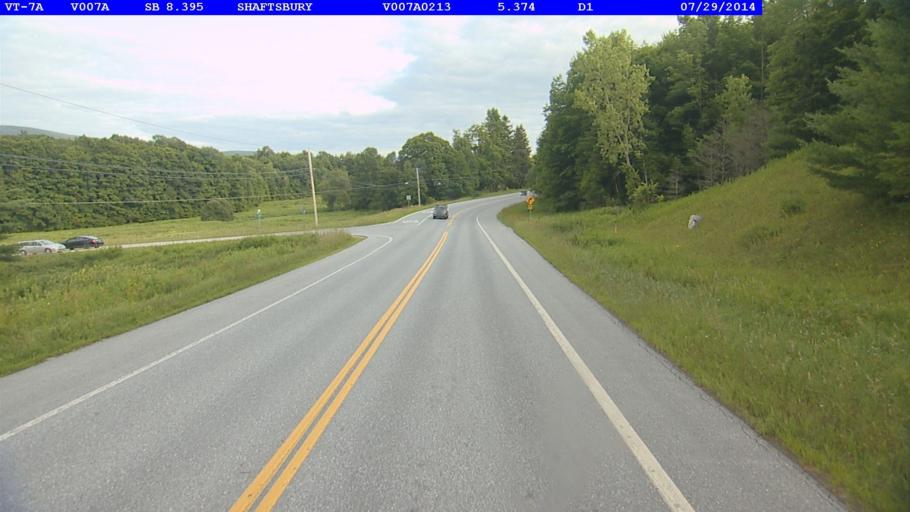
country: US
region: Vermont
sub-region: Bennington County
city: Arlington
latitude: 43.0075
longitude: -73.1950
